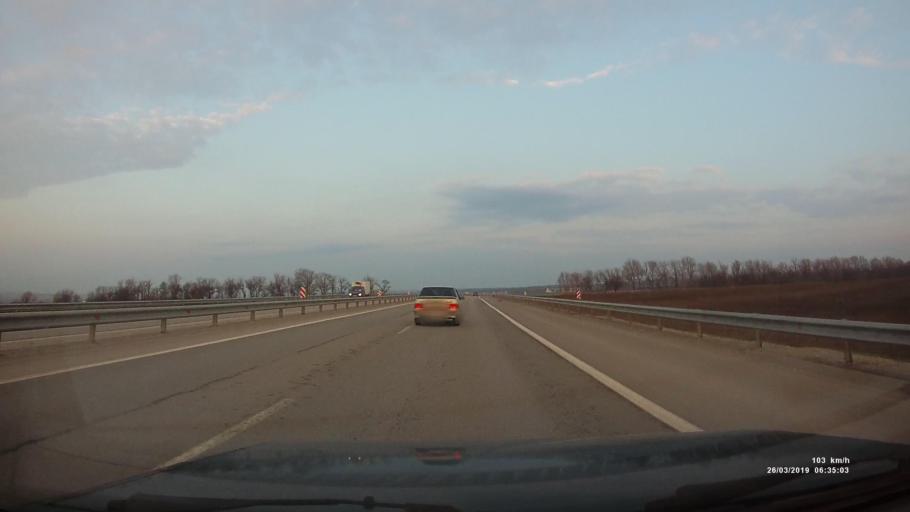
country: RU
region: Rostov
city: Chaltyr
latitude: 47.2786
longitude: 39.4539
